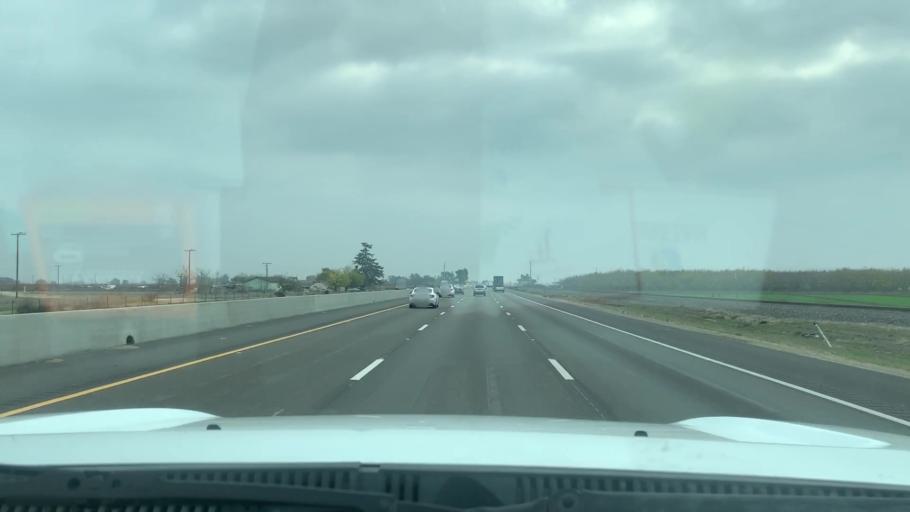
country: US
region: California
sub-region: Tulare County
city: Goshen
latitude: 36.2898
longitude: -119.3797
